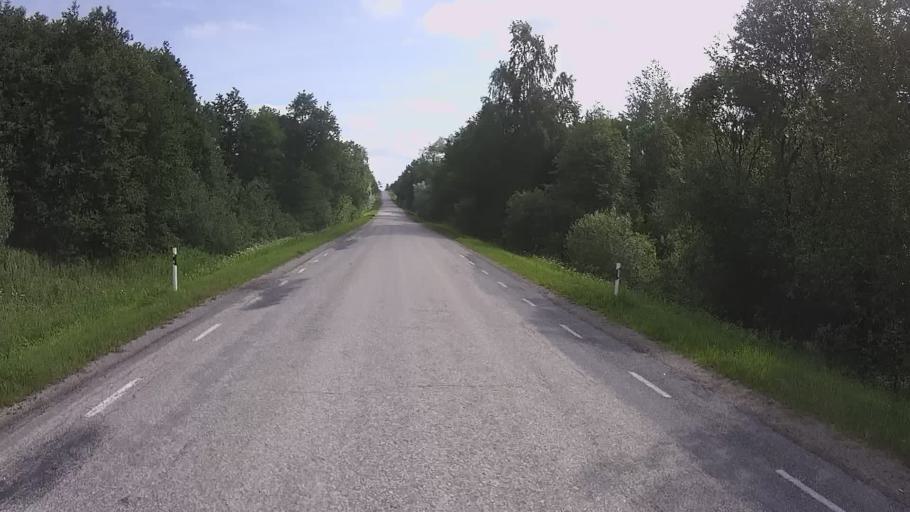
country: EE
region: Vorumaa
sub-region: Antsla vald
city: Vana-Antsla
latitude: 57.8528
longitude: 26.5875
